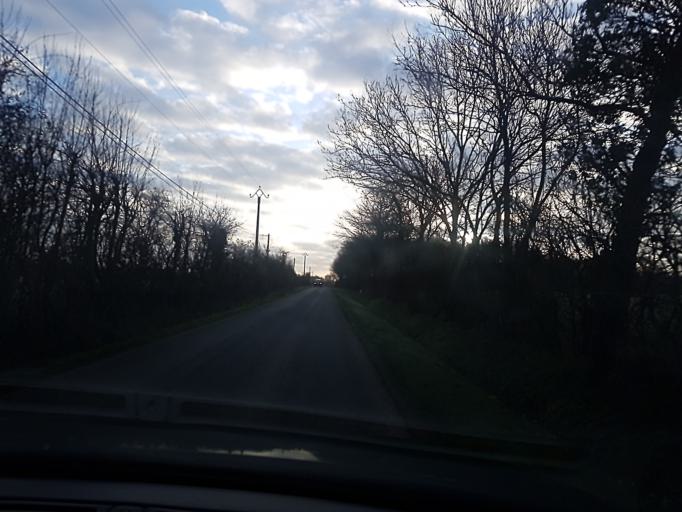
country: FR
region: Pays de la Loire
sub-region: Departement de la Loire-Atlantique
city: Ligne
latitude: 47.4049
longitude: -1.3891
